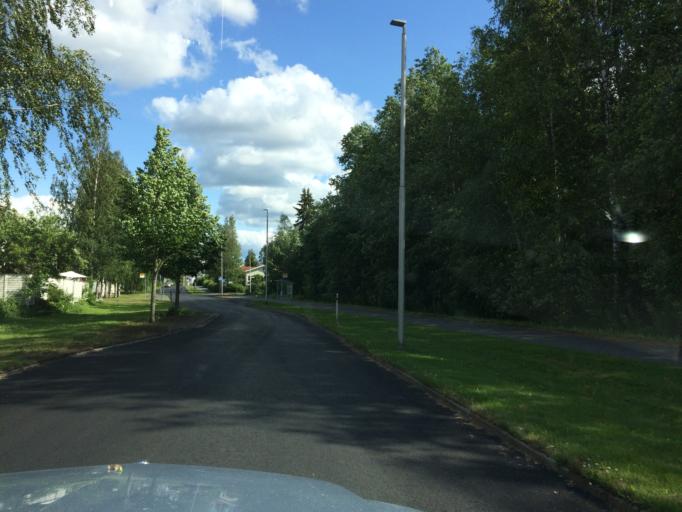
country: FI
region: Haeme
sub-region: Haemeenlinna
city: Haemeenlinna
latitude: 60.9856
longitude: 24.3979
